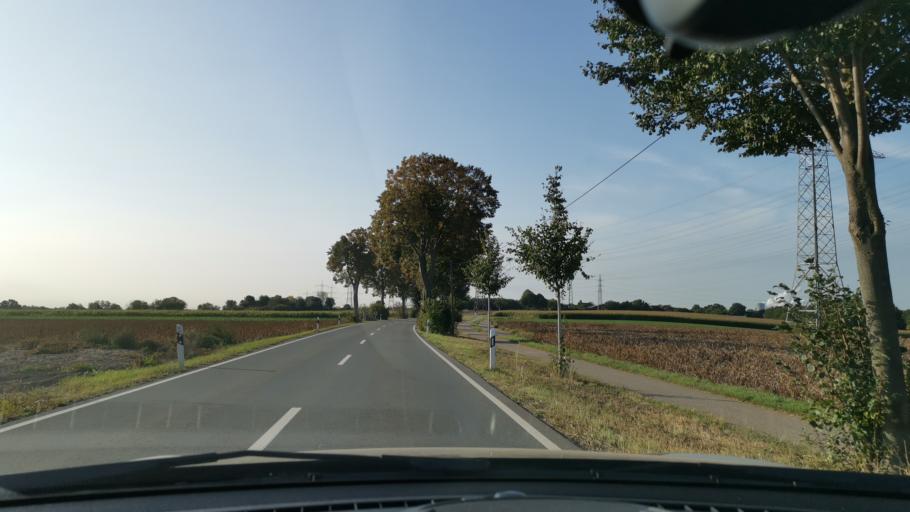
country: DE
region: North Rhine-Westphalia
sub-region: Regierungsbezirk Dusseldorf
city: Rommerskirchen
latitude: 51.0702
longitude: 6.7212
